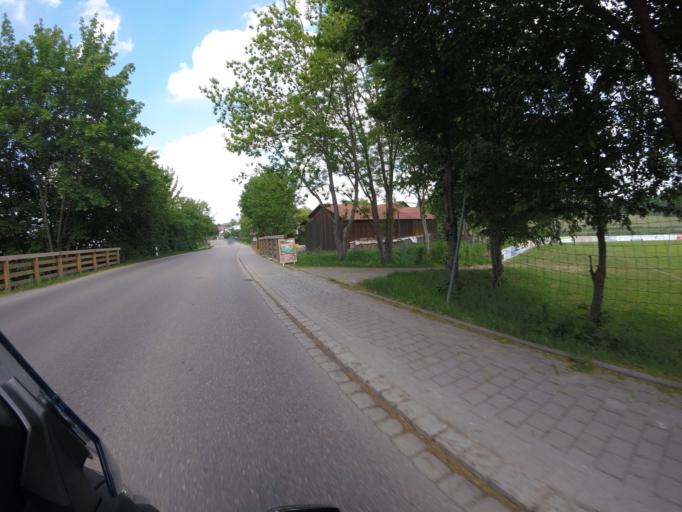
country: DE
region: Bavaria
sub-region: Upper Bavaria
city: Wolfersdorf
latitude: 48.4586
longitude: 11.7109
